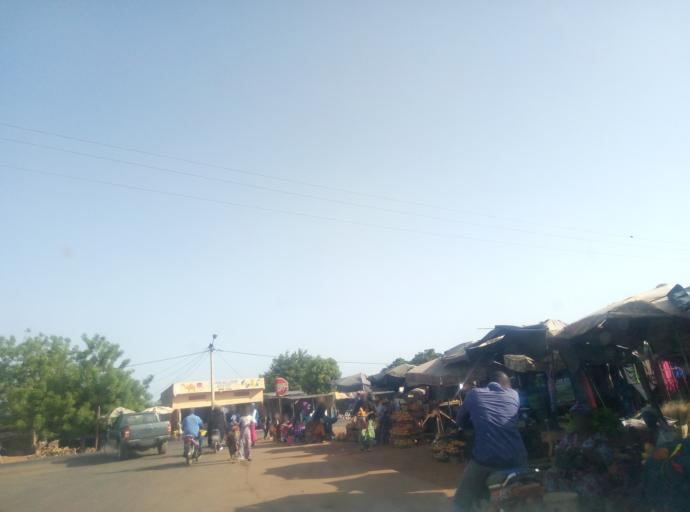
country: ML
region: Bamako
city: Bamako
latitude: 12.5875
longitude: -7.7665
